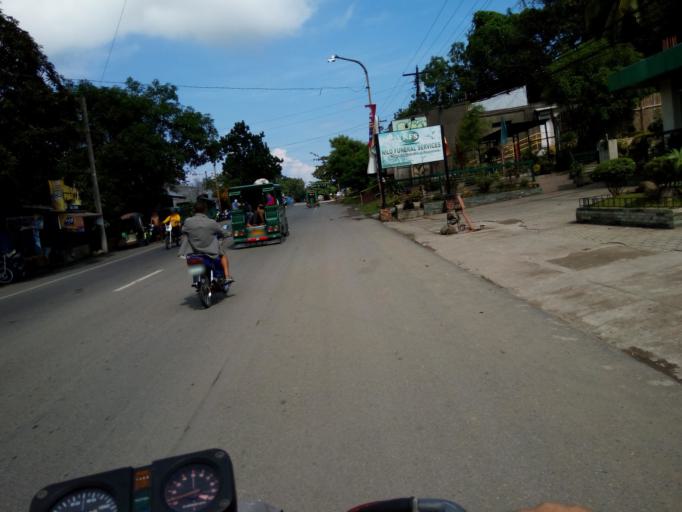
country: PH
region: Caraga
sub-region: Province of Surigao del Norte
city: Surigao
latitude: 9.7761
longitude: 125.4830
